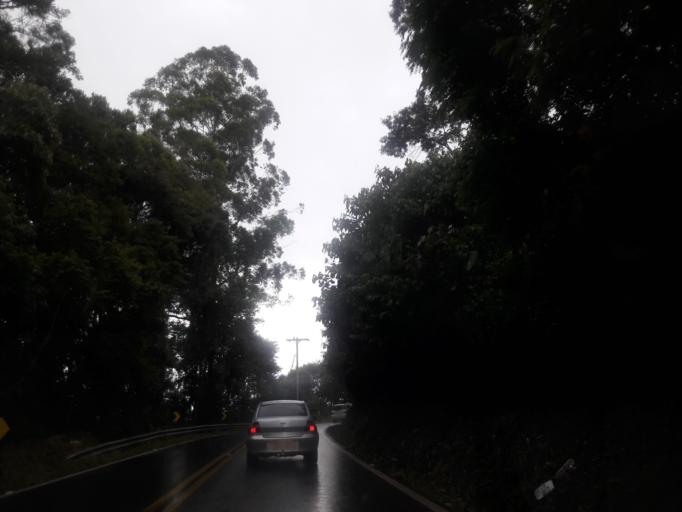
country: BR
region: Sao Paulo
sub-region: Aruja
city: Aruja
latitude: -23.3160
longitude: -46.4370
